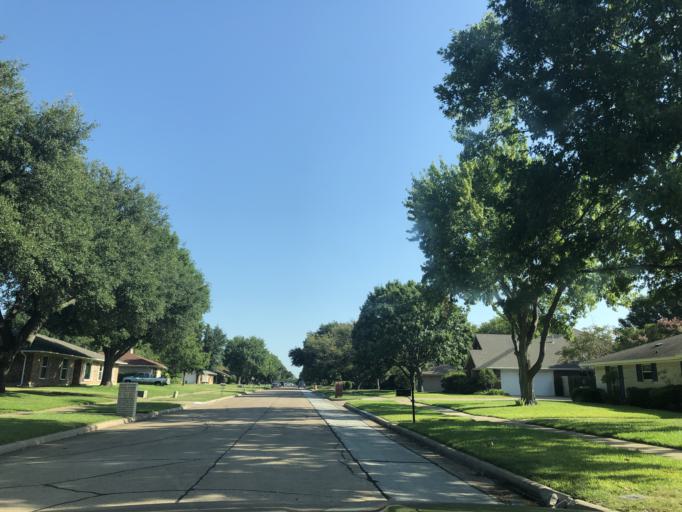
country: US
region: Texas
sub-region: Dallas County
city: Garland
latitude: 32.8654
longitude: -96.6408
